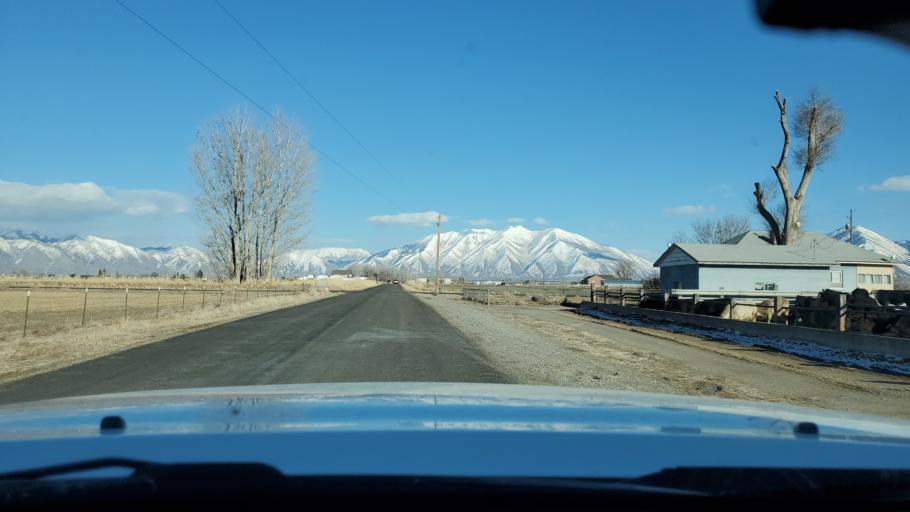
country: US
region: Utah
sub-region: Utah County
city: Benjamin
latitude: 40.1147
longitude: -111.7600
